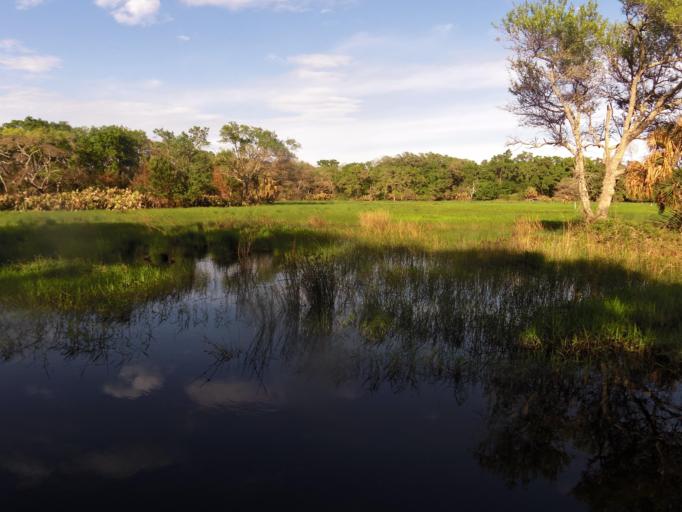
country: US
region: Florida
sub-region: Saint Johns County
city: Villano Beach
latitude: 30.0225
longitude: -81.3378
